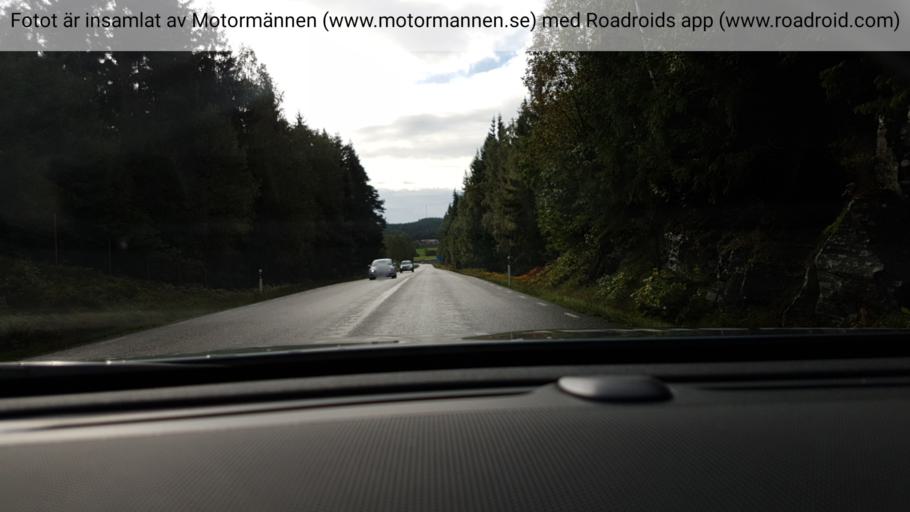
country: SE
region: Vaestra Goetaland
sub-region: Harryda Kommun
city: Ravlanda
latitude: 57.5606
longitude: 12.5163
